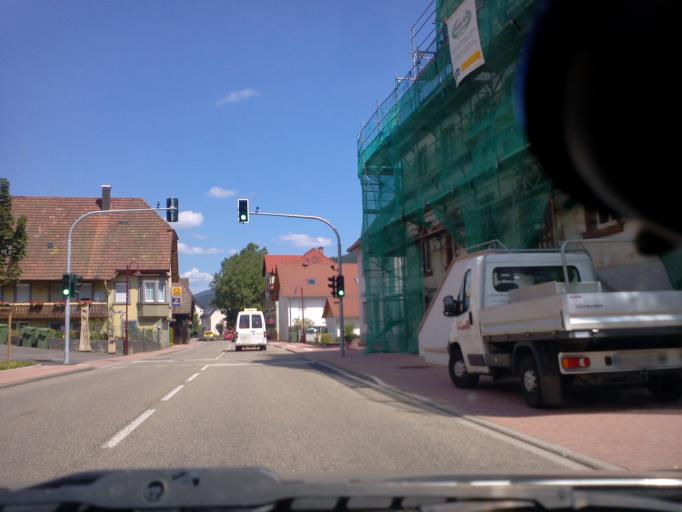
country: DE
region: Baden-Wuerttemberg
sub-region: Freiburg Region
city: Gutach (Schwarzwaldbahn)
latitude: 48.2475
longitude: 8.2116
